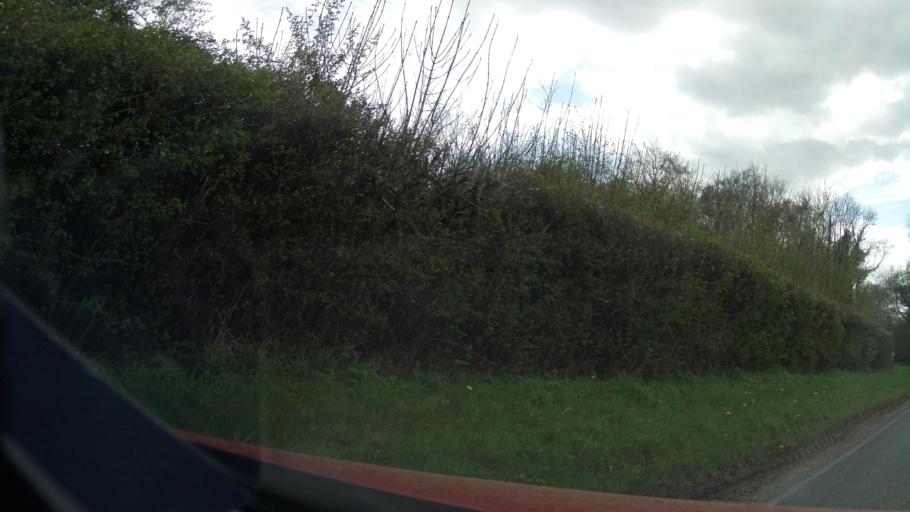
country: GB
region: England
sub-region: Hampshire
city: Andover
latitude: 51.2705
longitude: -1.4643
